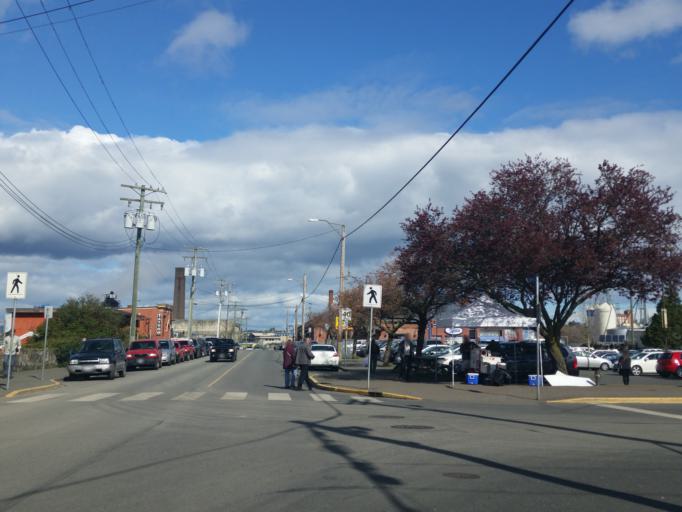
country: CA
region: British Columbia
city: Victoria
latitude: 48.4309
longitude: -123.3696
